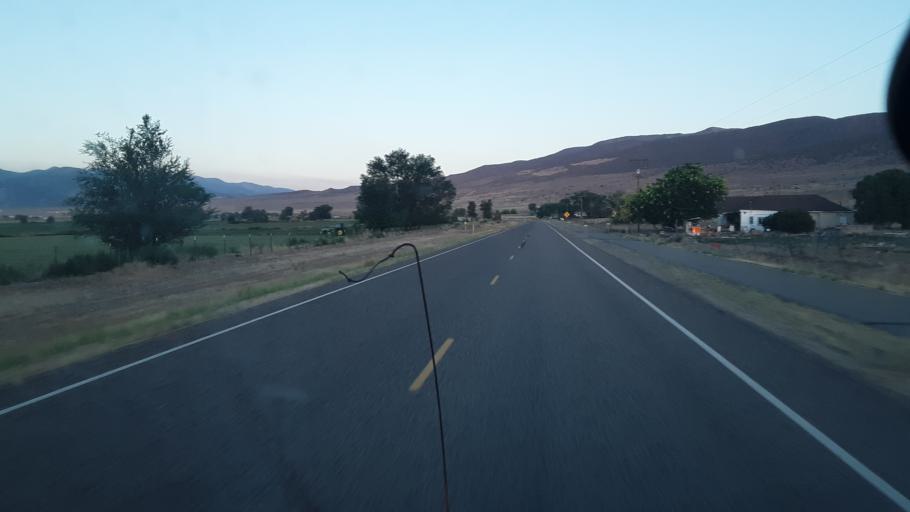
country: US
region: Utah
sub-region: Sevier County
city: Monroe
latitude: 38.6525
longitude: -112.2036
